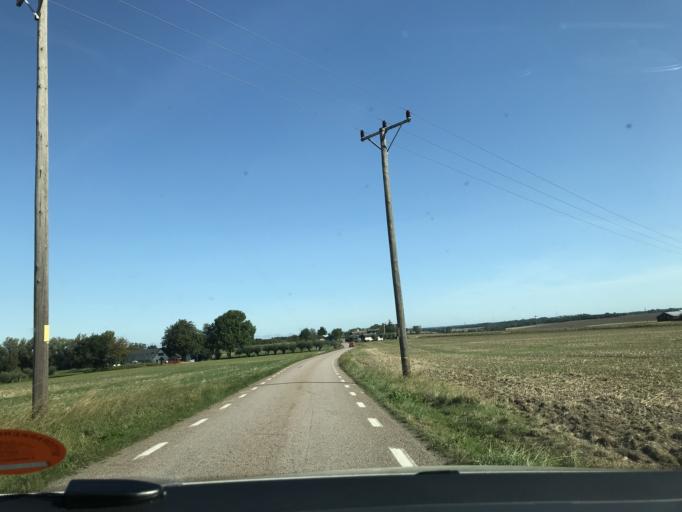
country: SE
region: Skane
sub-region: Landskrona
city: Asmundtorp
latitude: 55.9116
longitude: 12.9527
